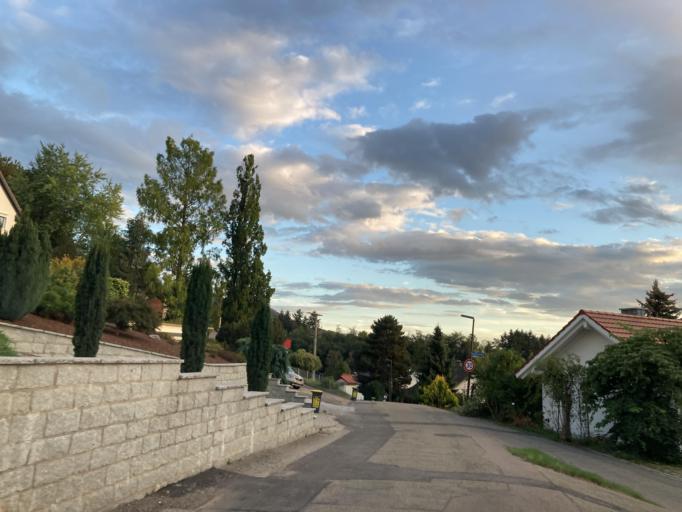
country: DE
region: Baden-Wuerttemberg
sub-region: Freiburg Region
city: Lauf
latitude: 48.6671
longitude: 8.1375
